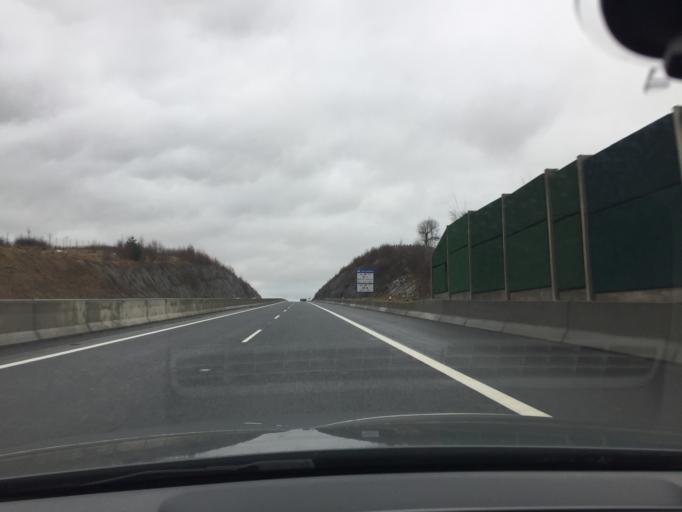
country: CZ
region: Ustecky
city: Chlumec
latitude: 50.7787
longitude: 13.9168
